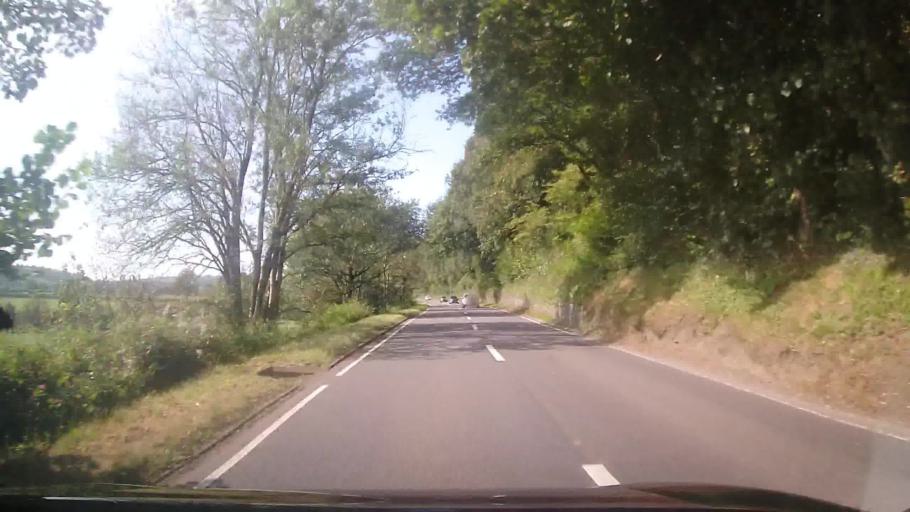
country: GB
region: Wales
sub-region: Carmarthenshire
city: Llanddarog
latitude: 51.8710
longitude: -4.2247
